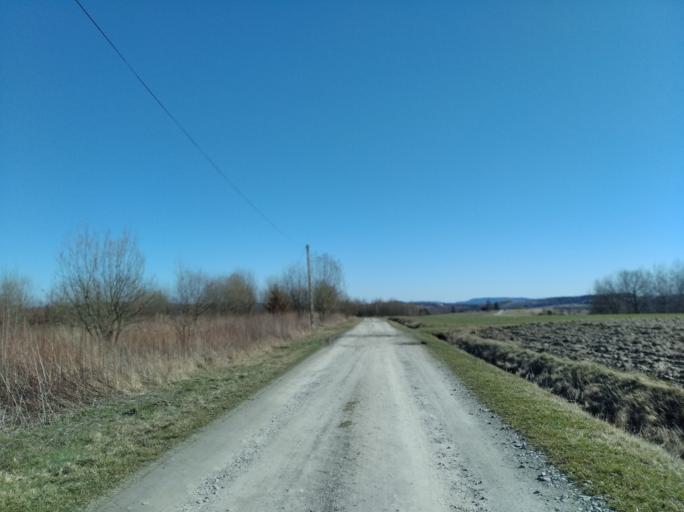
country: PL
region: Subcarpathian Voivodeship
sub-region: Powiat strzyzowski
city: Wisniowa
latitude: 49.9225
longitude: 21.6732
